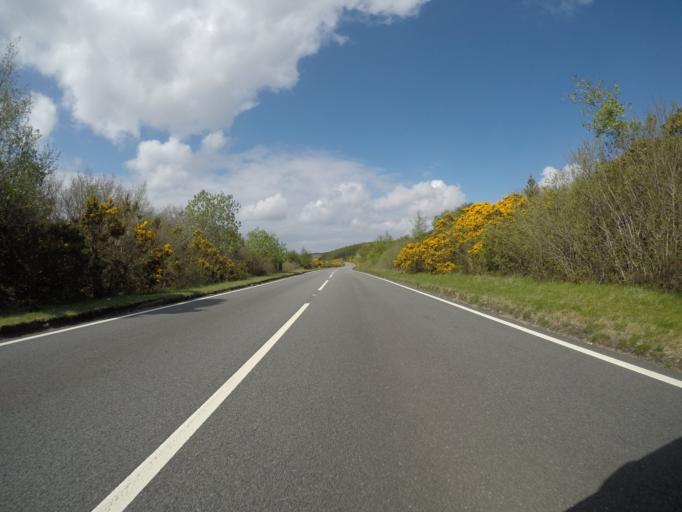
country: GB
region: Scotland
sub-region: Highland
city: Portree
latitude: 57.5210
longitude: -6.3414
